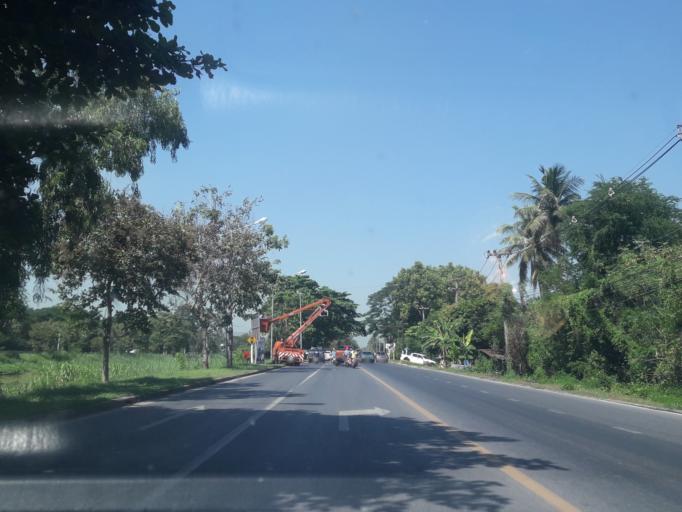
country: TH
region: Sara Buri
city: Nong Khae
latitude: 14.3363
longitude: 100.8675
